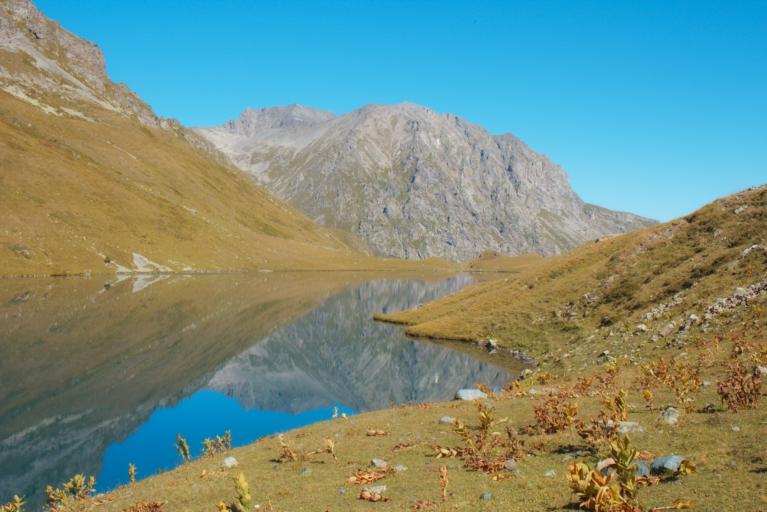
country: RU
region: Karachayevo-Cherkesiya
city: Mednogorskiy
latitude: 43.6148
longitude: 41.1527
